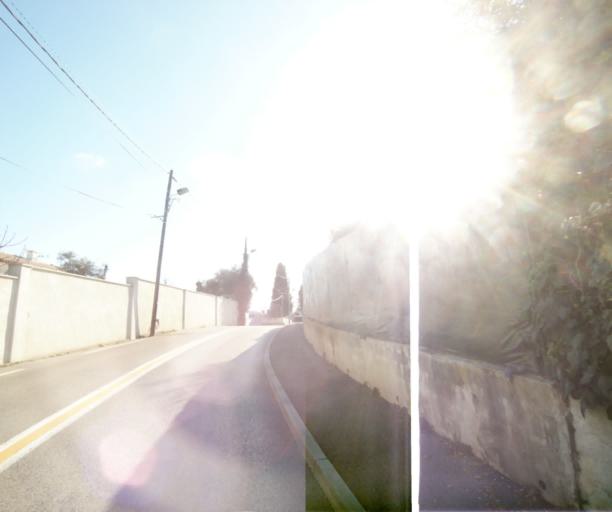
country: FR
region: Provence-Alpes-Cote d'Azur
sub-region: Departement des Alpes-Maritimes
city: Biot
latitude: 43.6023
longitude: 7.1067
